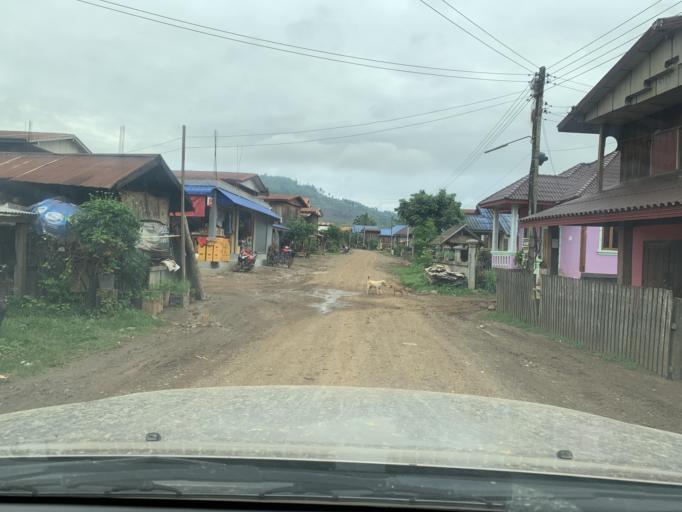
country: TH
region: Nan
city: Mae Charim
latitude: 18.4208
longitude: 101.4484
